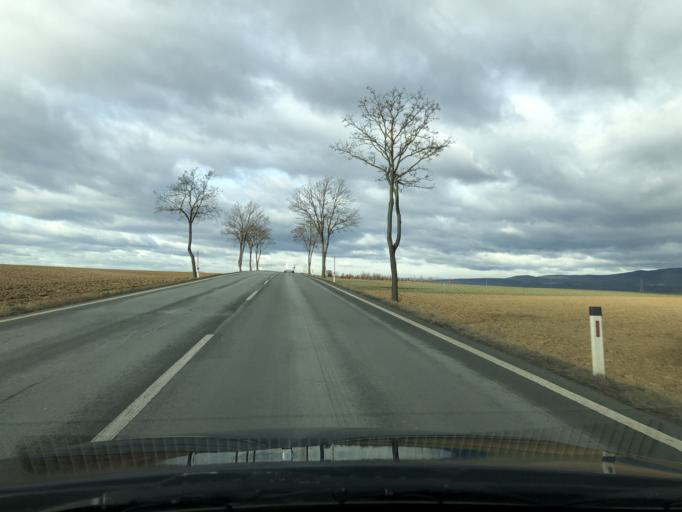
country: AT
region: Burgenland
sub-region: Politischer Bezirk Oberwart
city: Schachendorf
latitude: 47.2600
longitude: 16.4560
